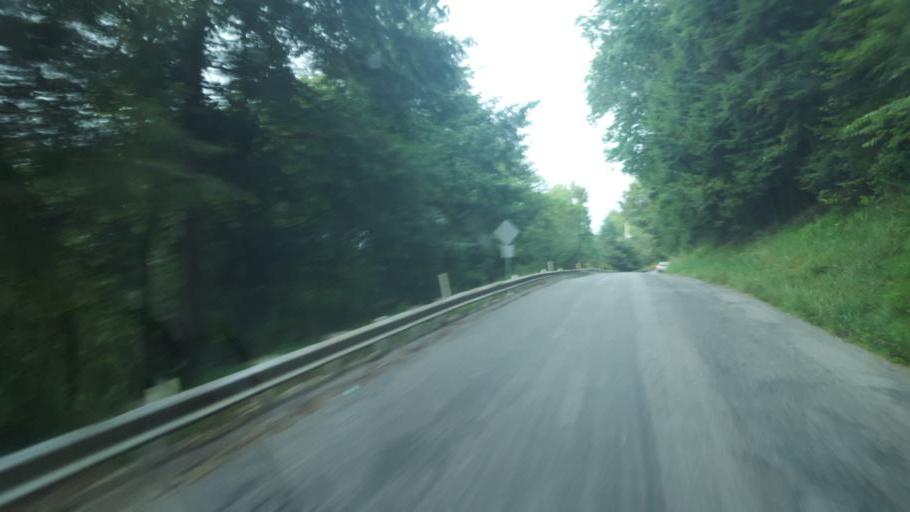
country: US
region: Pennsylvania
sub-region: Clarion County
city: Knox
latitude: 41.1613
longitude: -79.5364
